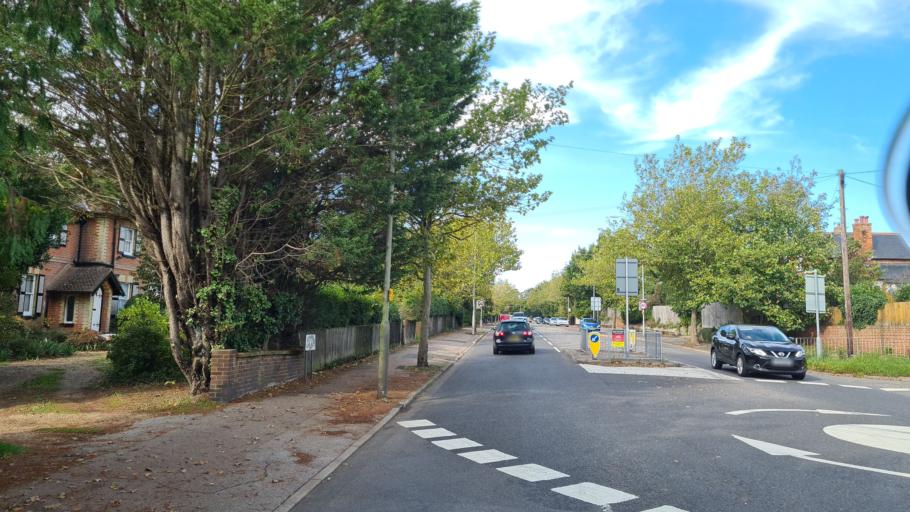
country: GB
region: England
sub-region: East Sussex
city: Saint Leonards-on-Sea
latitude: 50.8772
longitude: 0.5564
